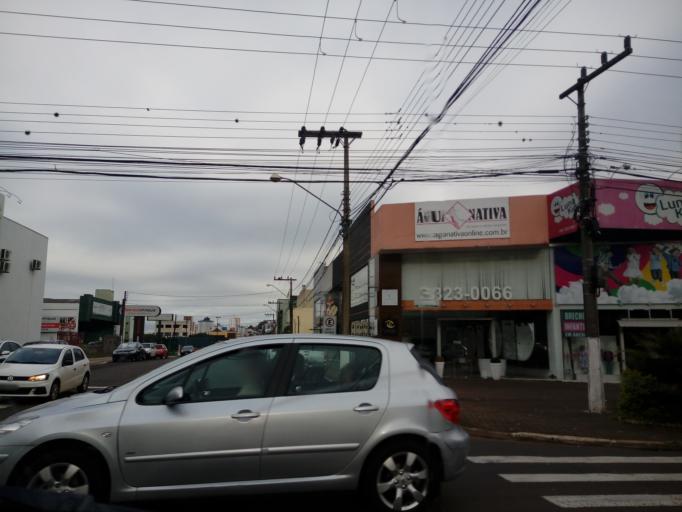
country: BR
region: Santa Catarina
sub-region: Chapeco
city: Chapeco
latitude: -27.0910
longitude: -52.6182
